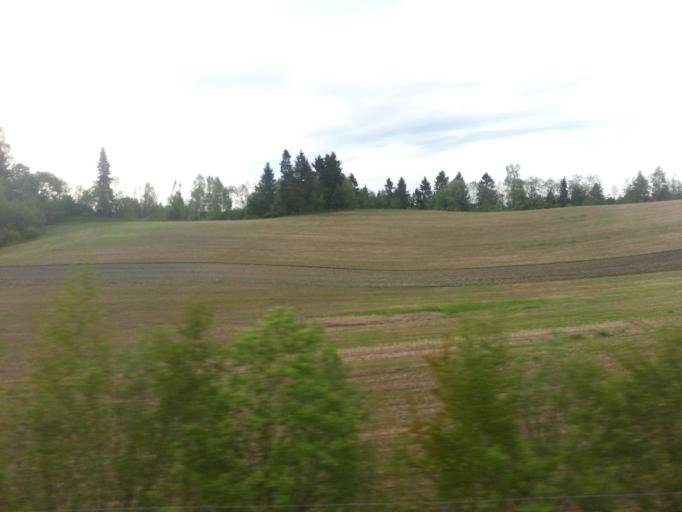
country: NO
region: Akershus
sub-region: Eidsvoll
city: Eidsvoll
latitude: 60.3142
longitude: 11.2348
